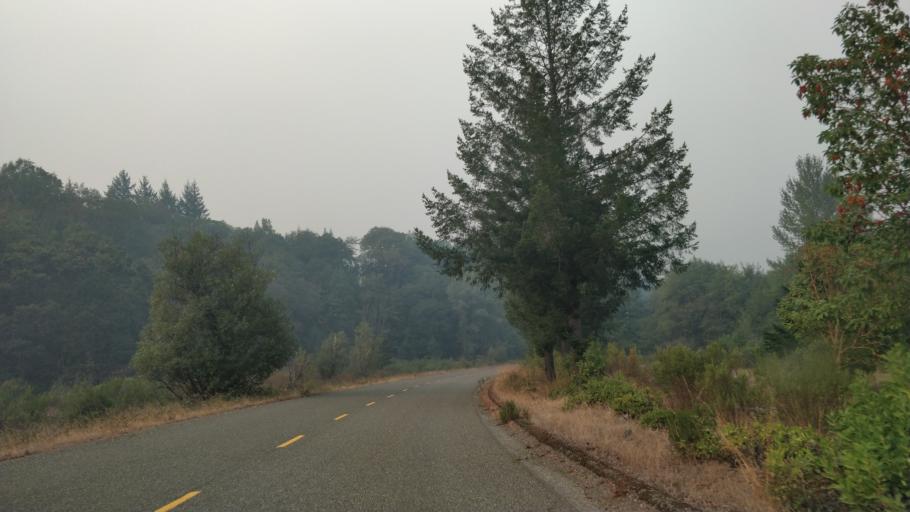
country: US
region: California
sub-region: Humboldt County
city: Rio Dell
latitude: 40.3369
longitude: -124.0272
